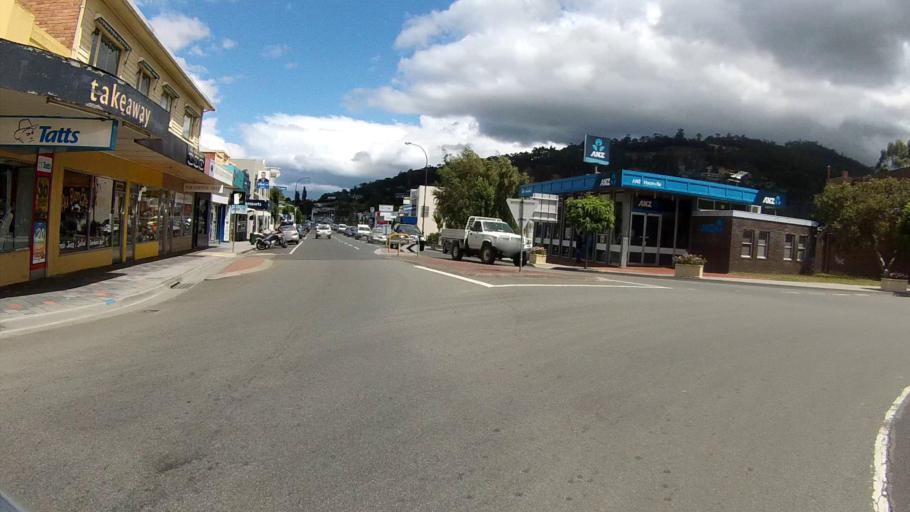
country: AU
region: Tasmania
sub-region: Huon Valley
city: Huonville
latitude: -43.0309
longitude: 147.0486
